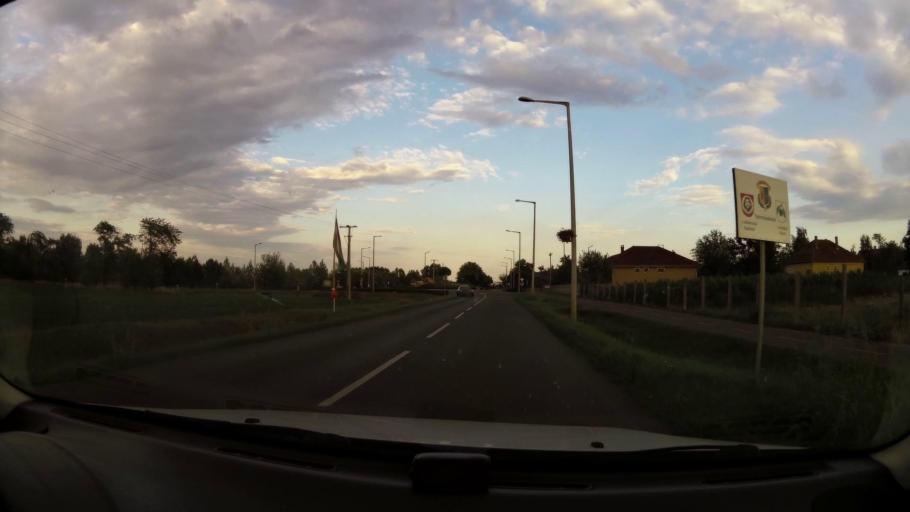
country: HU
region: Pest
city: Ujszilvas
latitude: 47.2788
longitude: 19.9231
